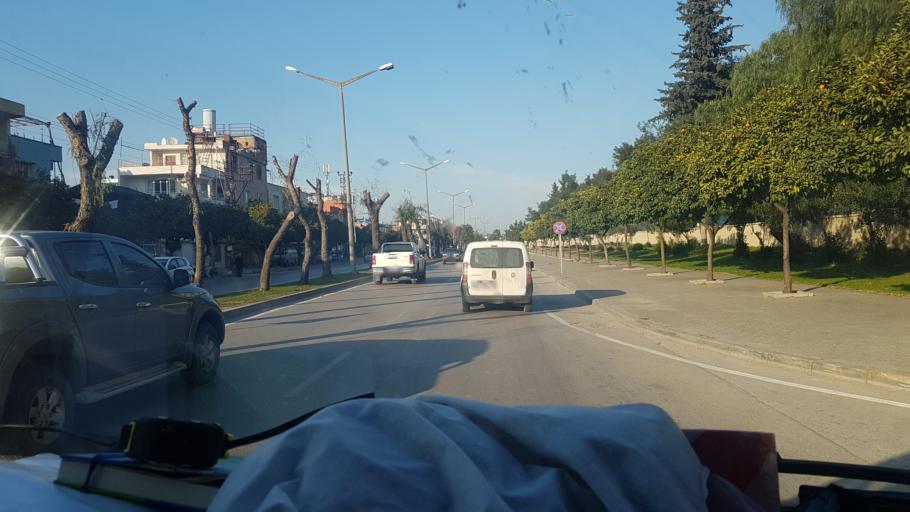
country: TR
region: Adana
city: Adana
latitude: 37.0159
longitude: 35.3398
